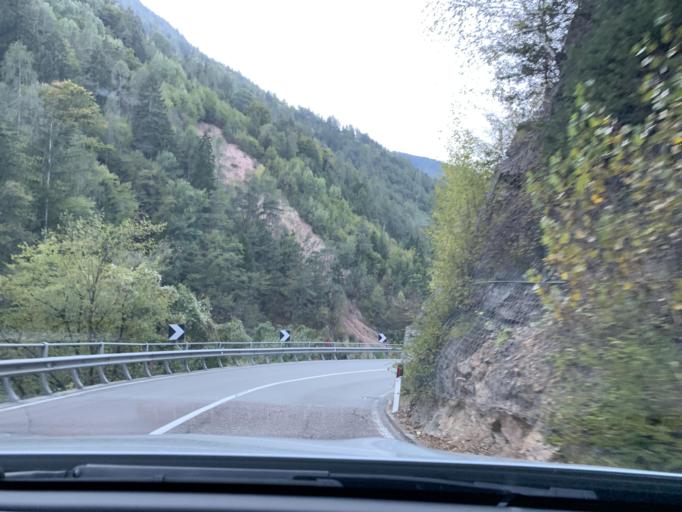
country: IT
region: Trentino-Alto Adige
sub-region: Bolzano
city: Cornedo All'Isarco
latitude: 46.4601
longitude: 11.4170
